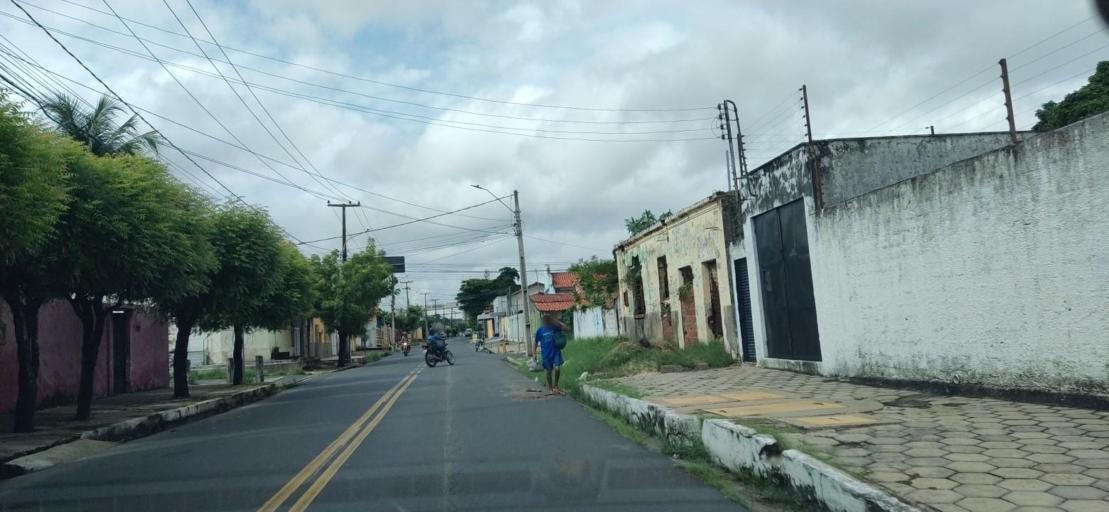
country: BR
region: Piaui
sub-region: Teresina
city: Teresina
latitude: -5.0783
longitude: -42.8064
